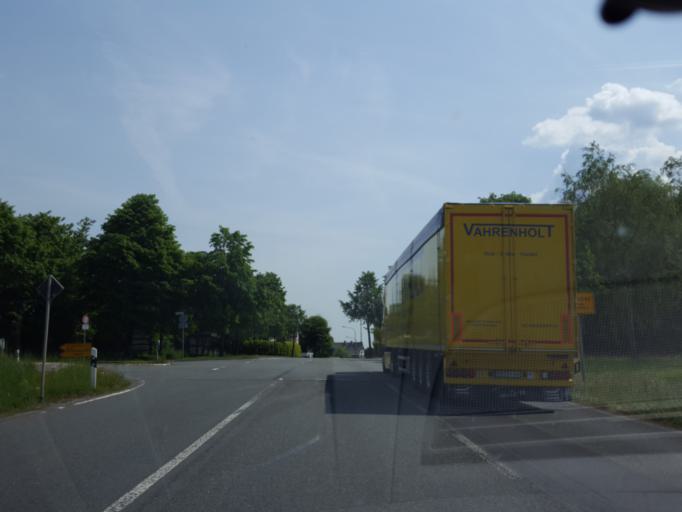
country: DE
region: North Rhine-Westphalia
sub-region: Regierungsbezirk Arnsberg
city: Olsberg
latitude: 51.3859
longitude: 8.4972
